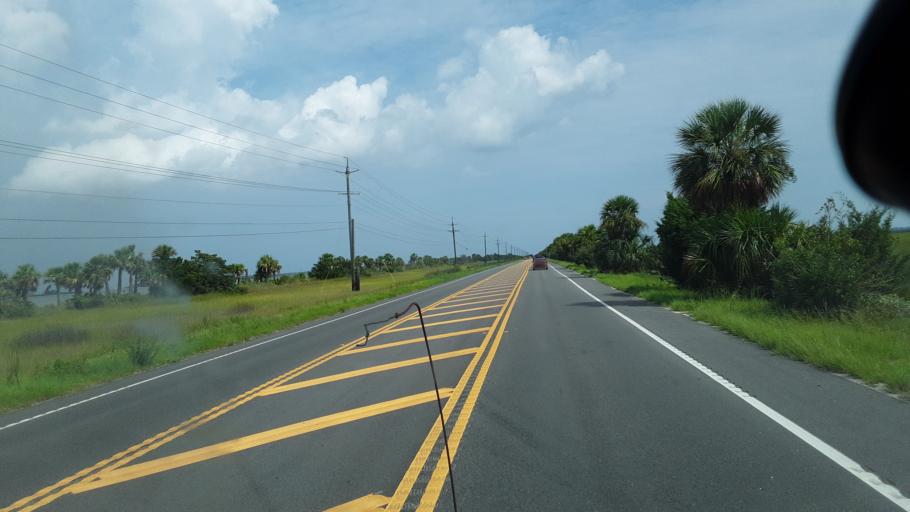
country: US
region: Georgia
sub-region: Chatham County
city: Wilmington Island
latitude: 32.0373
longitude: -80.9412
